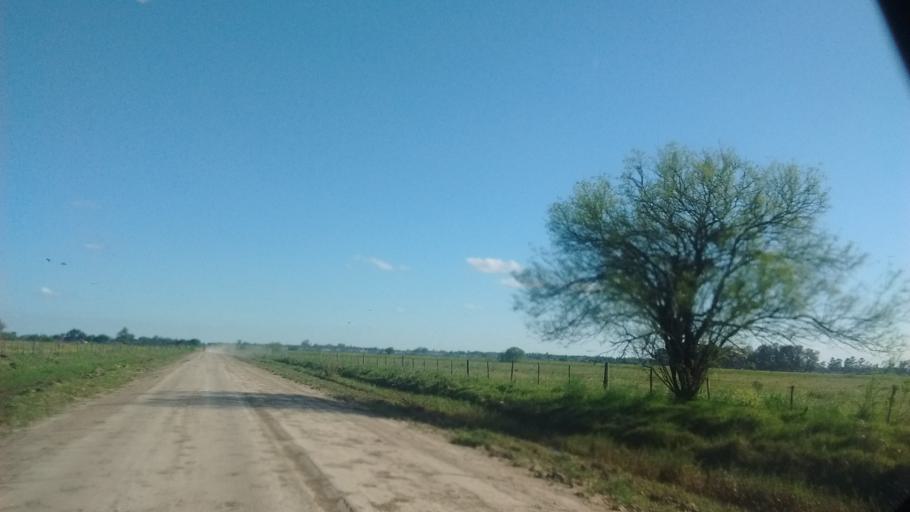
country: AR
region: Santa Fe
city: Funes
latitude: -32.8825
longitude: -60.7982
